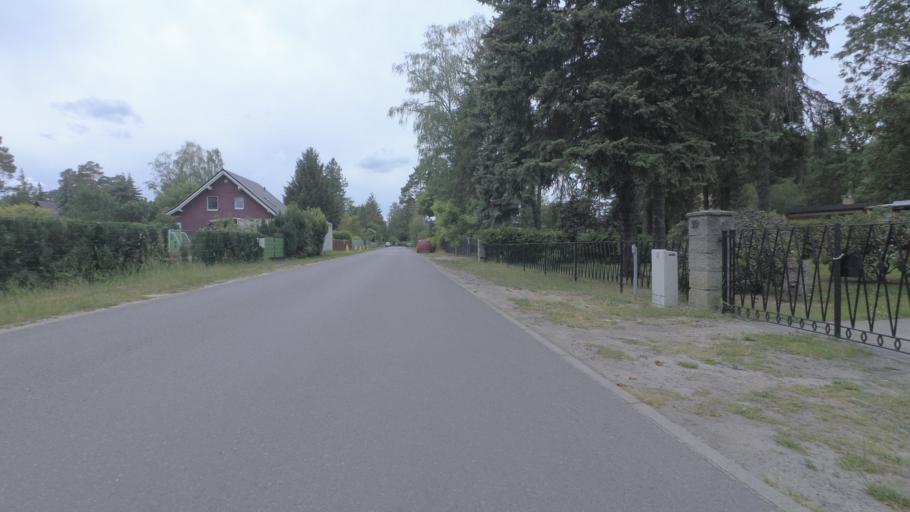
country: DE
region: Brandenburg
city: Bestensee
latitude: 52.2721
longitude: 13.7507
